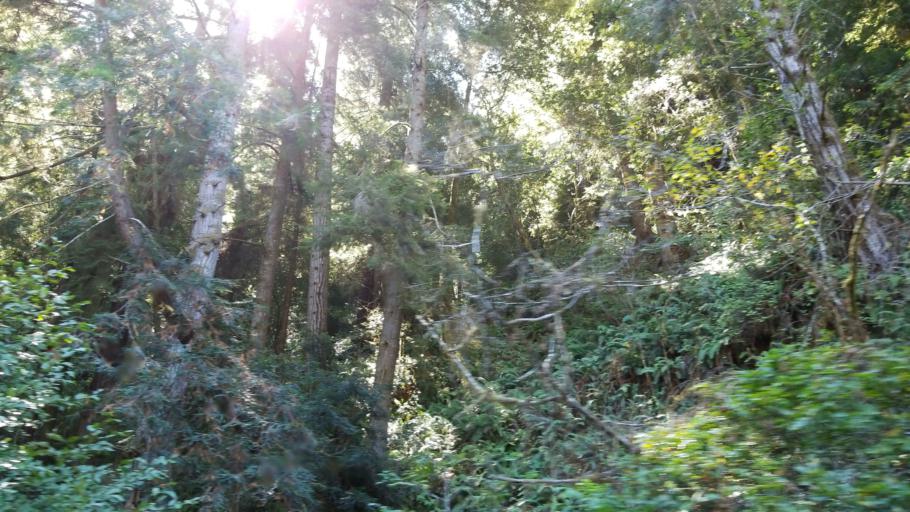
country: US
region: California
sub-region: Mendocino County
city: Fort Bragg
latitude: 39.4475
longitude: -123.7721
